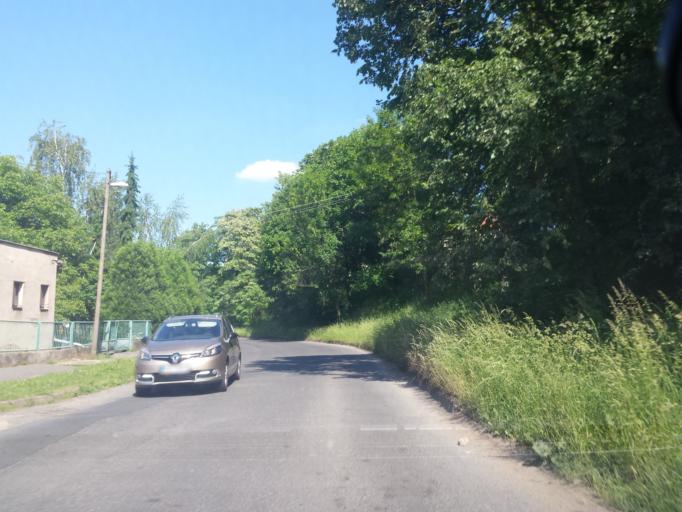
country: CZ
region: Central Bohemia
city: Nelahozeves
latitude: 50.2608
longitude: 14.2989
